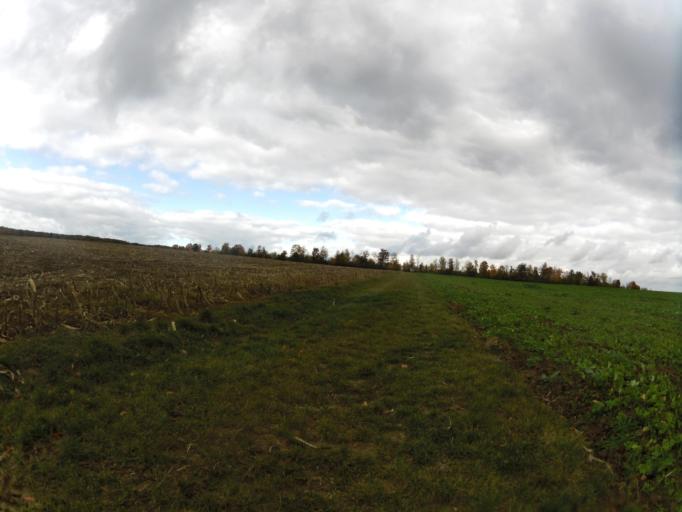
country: DE
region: Bavaria
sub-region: Regierungsbezirk Unterfranken
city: Kurnach
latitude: 49.8714
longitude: 10.0019
